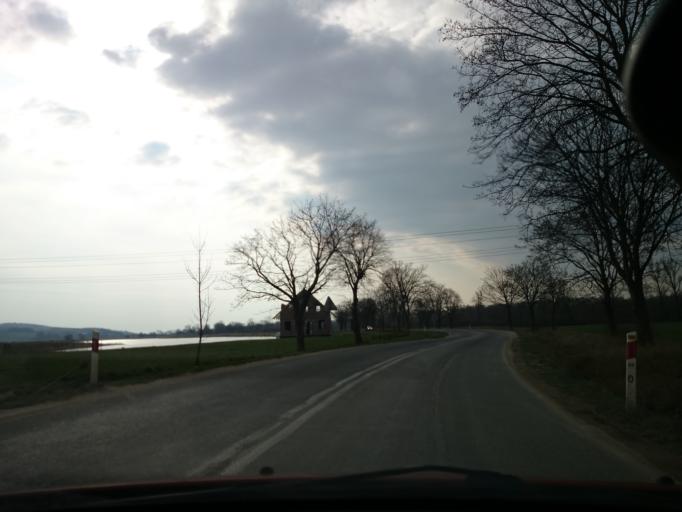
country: PL
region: Lower Silesian Voivodeship
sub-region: Powiat zabkowicki
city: Kamieniec Zabkowicki
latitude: 50.5199
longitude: 16.9118
